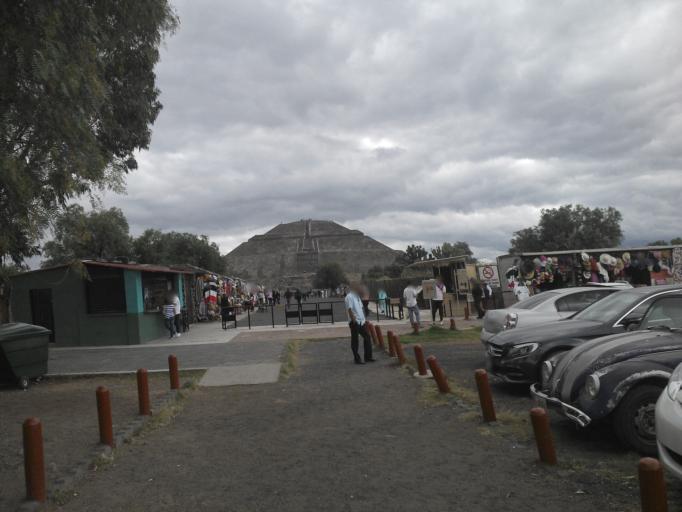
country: MX
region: Mexico
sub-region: Teotihuacan
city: Teotihuacan de Arista
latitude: 19.6934
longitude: -98.8479
